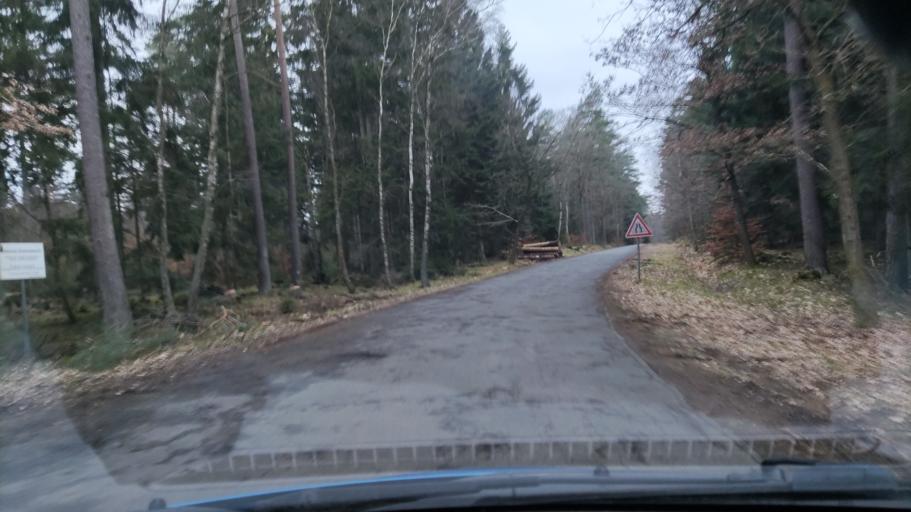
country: DE
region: Lower Saxony
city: Rehlingen
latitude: 53.0562
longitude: 10.2187
